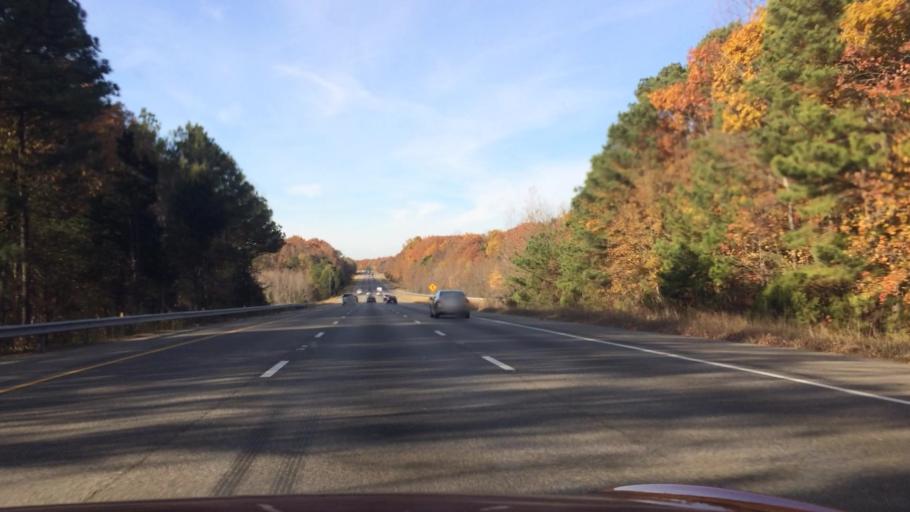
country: US
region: Virginia
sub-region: Henrico County
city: Glen Allen
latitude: 37.6805
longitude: -77.5430
